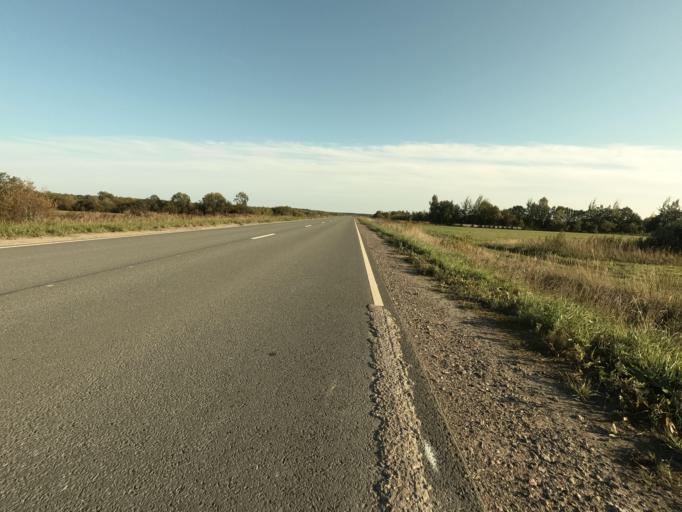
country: RU
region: St.-Petersburg
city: Sapernyy
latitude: 59.7470
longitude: 30.6430
